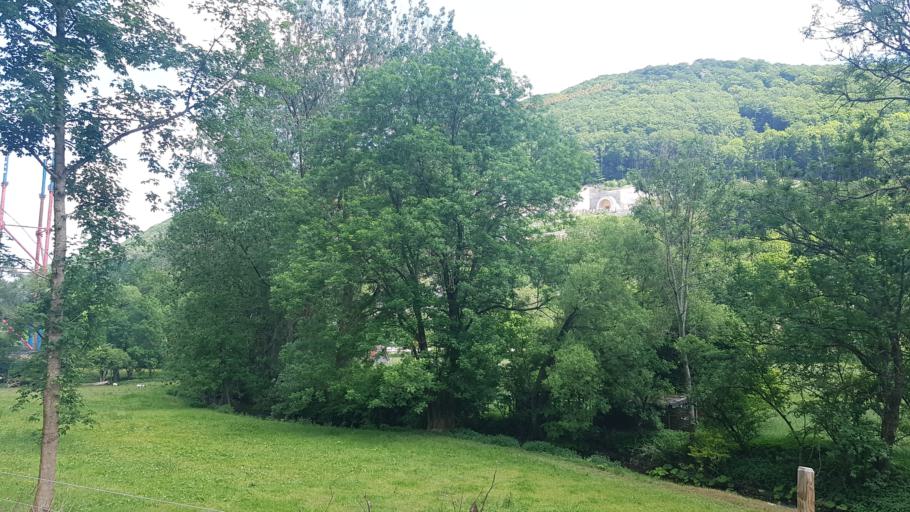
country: DE
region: Baden-Wuerttemberg
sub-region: Regierungsbezirk Stuttgart
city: Muhlhausen
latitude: 48.5706
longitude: 9.6427
